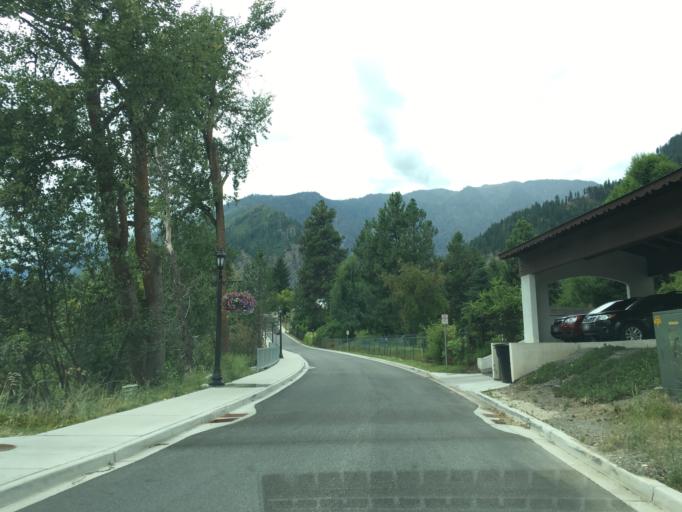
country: US
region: Washington
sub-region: Chelan County
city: Leavenworth
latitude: 47.5938
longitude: -120.6643
